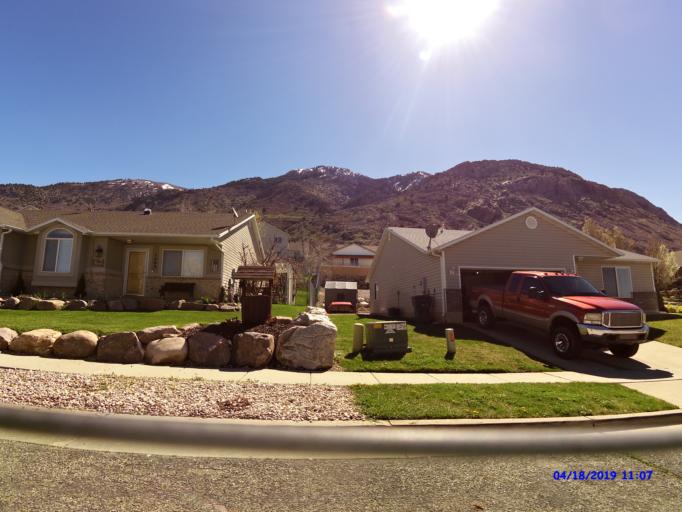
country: US
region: Utah
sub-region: Weber County
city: North Ogden
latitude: 41.2840
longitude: -111.9508
